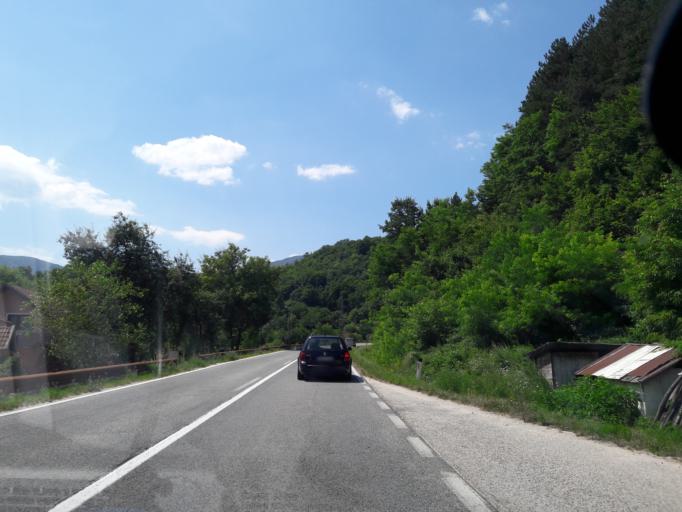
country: BA
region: Republika Srpska
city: Mrkonjic Grad
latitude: 44.3769
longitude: 17.1318
